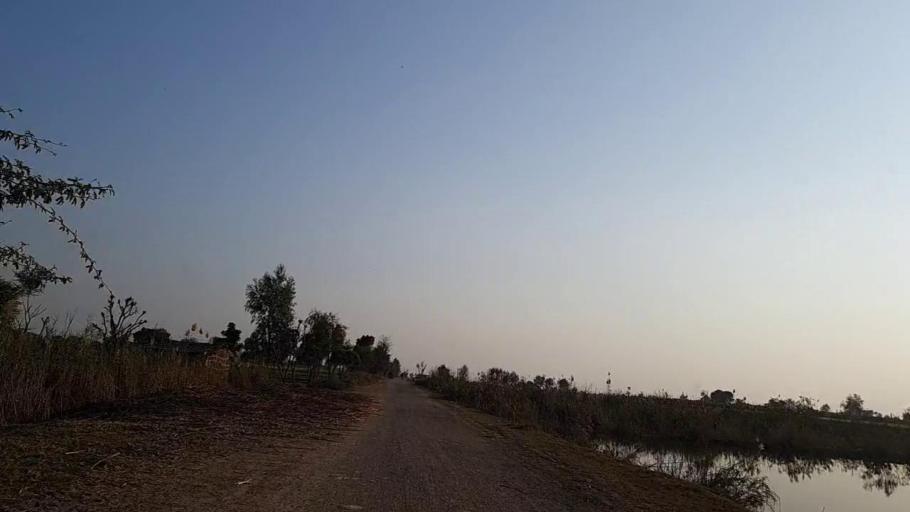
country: PK
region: Sindh
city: Sakrand
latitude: 26.0395
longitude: 68.4378
